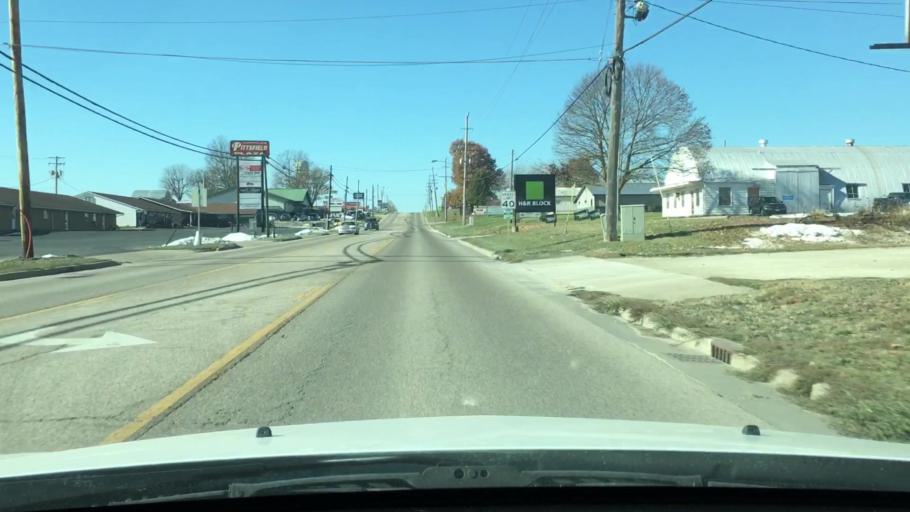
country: US
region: Illinois
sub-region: Pike County
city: Pittsfield
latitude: 39.6047
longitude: -90.8326
